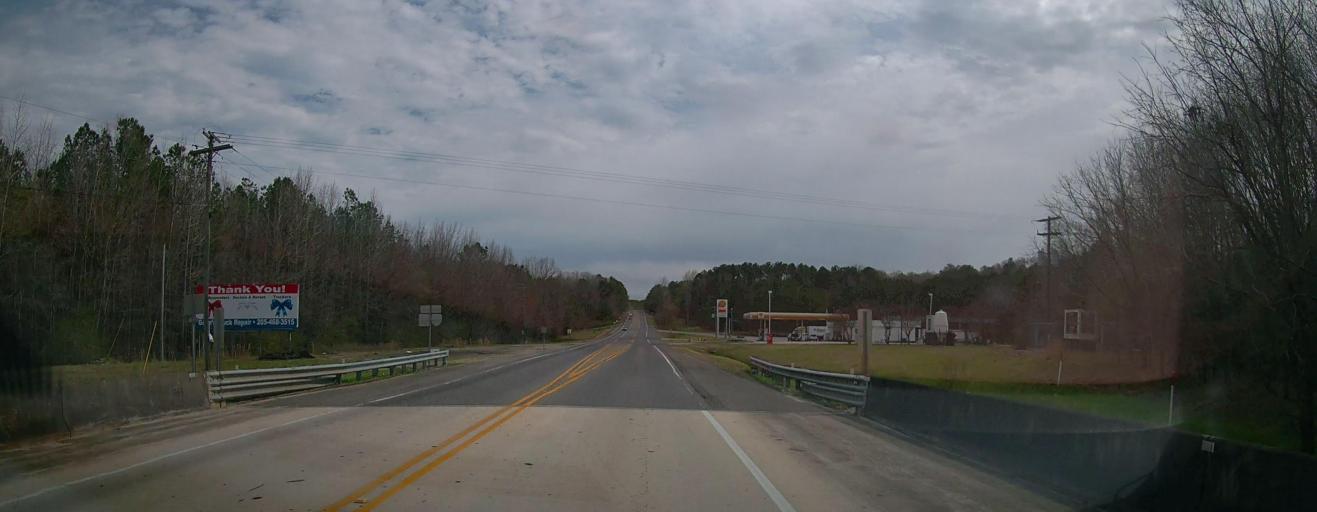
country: US
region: Alabama
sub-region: Marion County
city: Hamilton
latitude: 34.0694
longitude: -87.9740
